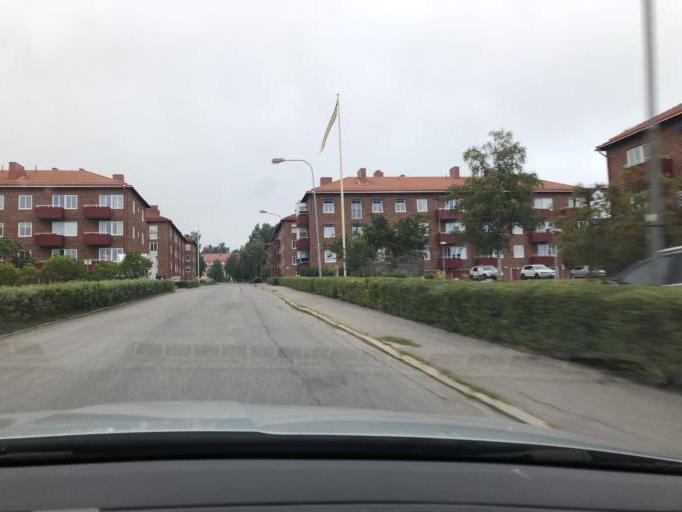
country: SE
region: Vaesternorrland
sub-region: Sundsvalls Kommun
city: Sundsvall
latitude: 62.3995
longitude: 17.3199
